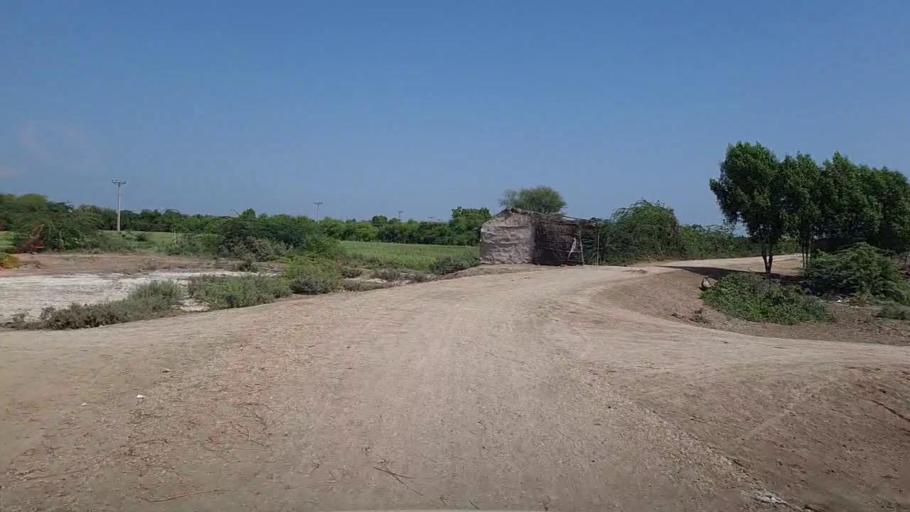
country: PK
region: Sindh
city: Talhar
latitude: 24.8347
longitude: 68.7212
